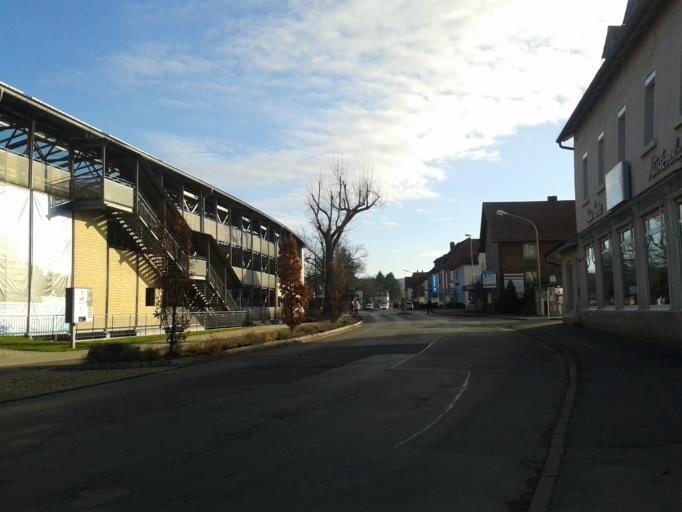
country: DE
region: Bavaria
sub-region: Upper Franconia
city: Kronach
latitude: 50.2373
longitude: 11.3262
